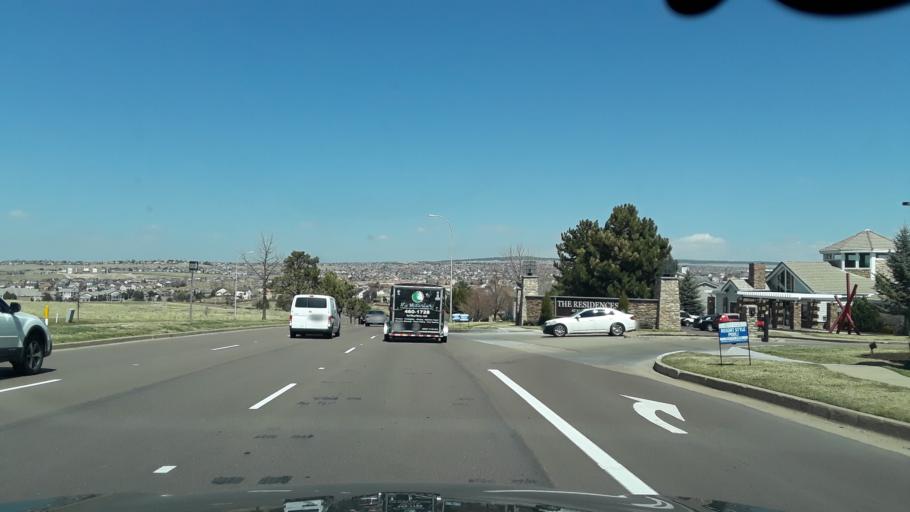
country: US
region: Colorado
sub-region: El Paso County
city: Cimarron Hills
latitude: 38.9226
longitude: -104.7384
